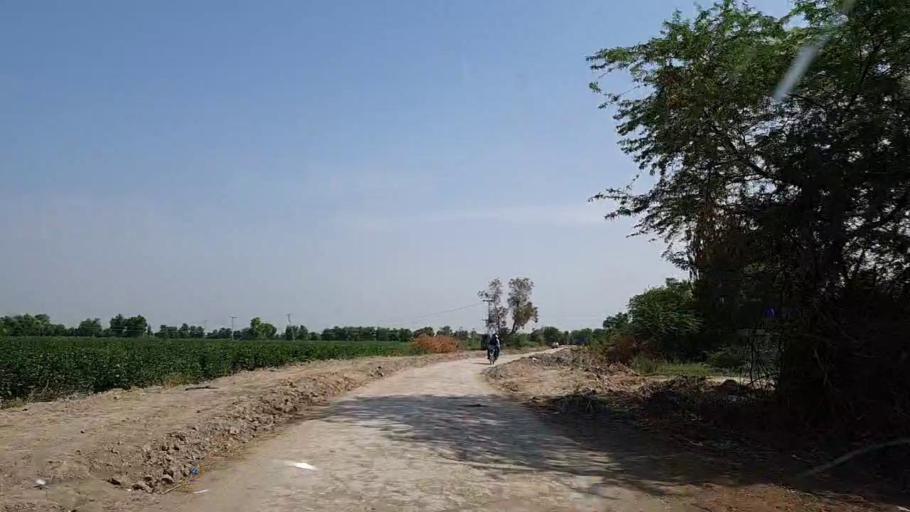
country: PK
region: Sindh
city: Khanpur
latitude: 27.7473
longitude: 69.3411
